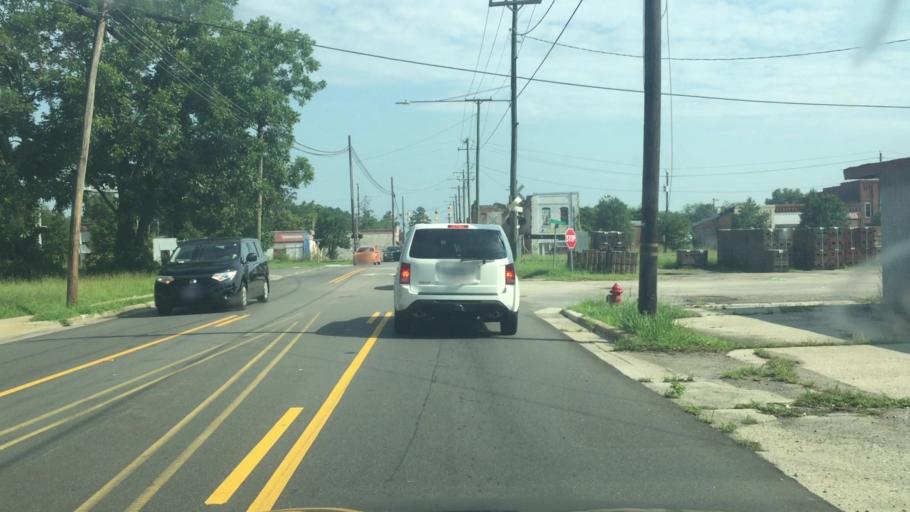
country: US
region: North Carolina
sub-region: Columbus County
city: Chadbourn
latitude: 34.3216
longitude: -78.8264
